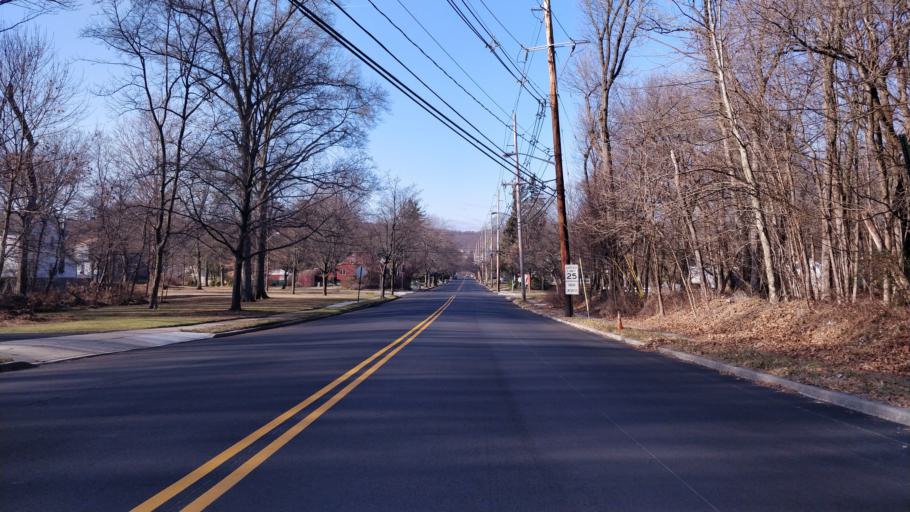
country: US
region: New Jersey
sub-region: Middlesex County
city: Dunellen
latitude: 40.6056
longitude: -74.4501
